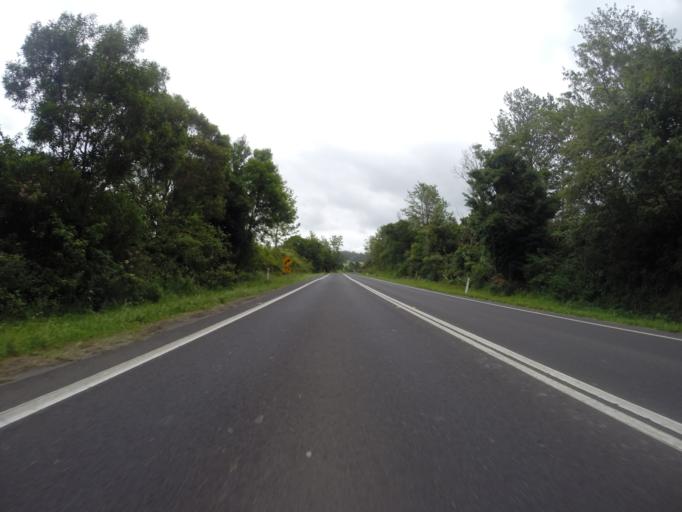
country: AU
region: New South Wales
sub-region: Kiama
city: Gerringong
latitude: -34.7458
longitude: 150.7595
